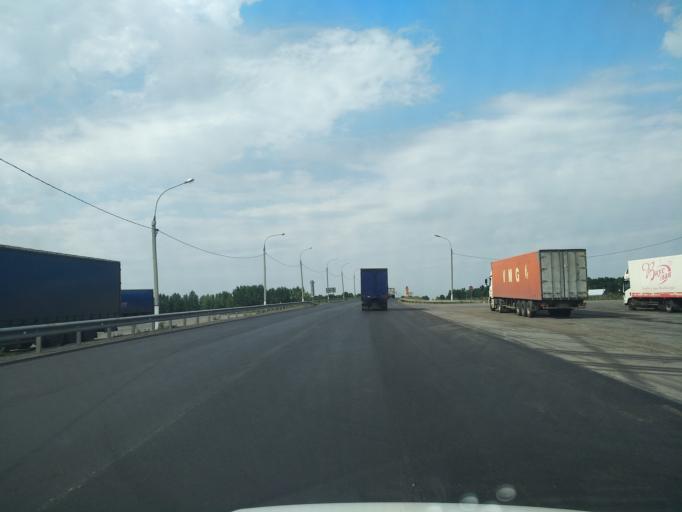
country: RU
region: Voronezj
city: Pereleshino
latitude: 51.7645
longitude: 40.1311
